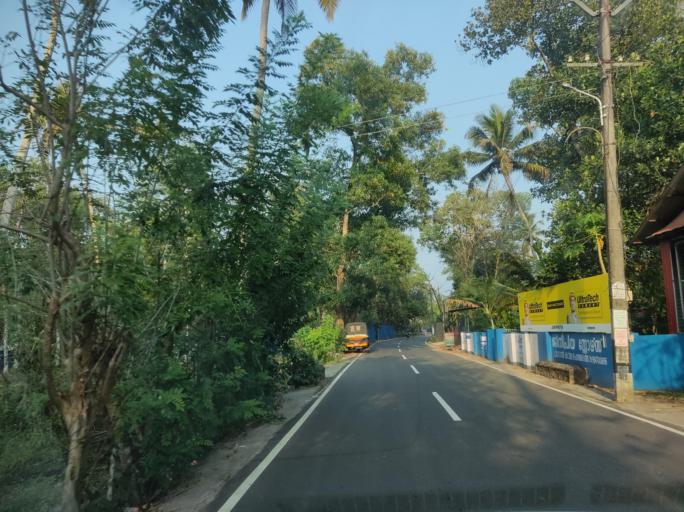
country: IN
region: Kerala
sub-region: Alappuzha
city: Alleppey
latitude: 9.5905
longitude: 76.3083
